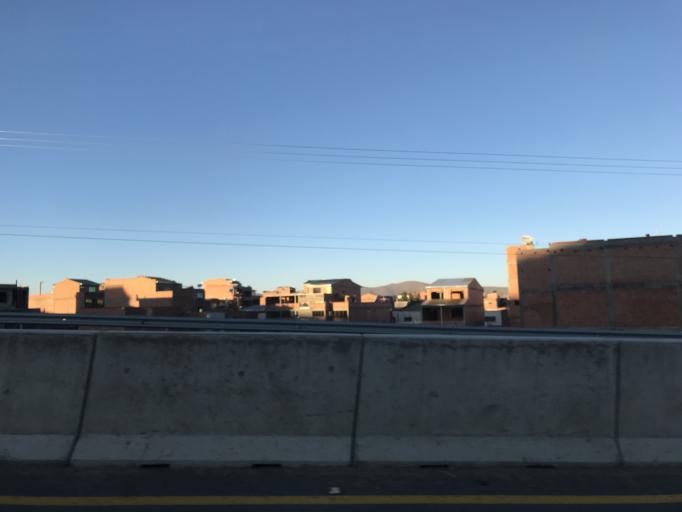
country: BO
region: La Paz
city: Batallas
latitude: -16.2978
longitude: -68.5304
